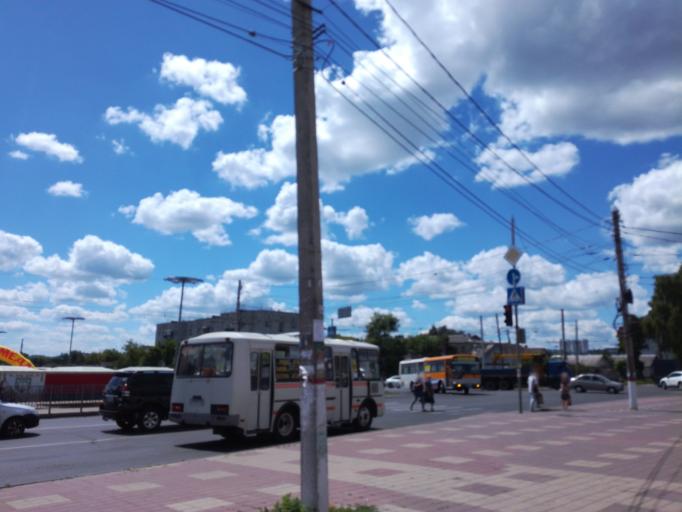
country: RU
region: Kursk
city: Kursk
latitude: 51.7562
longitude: 36.2237
